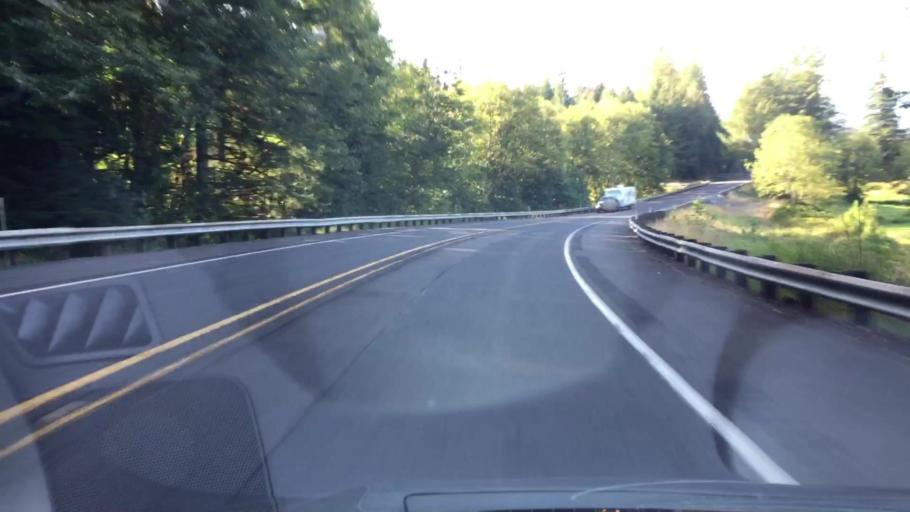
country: US
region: Washington
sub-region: Lewis County
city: Morton
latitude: 46.5219
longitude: -122.2254
